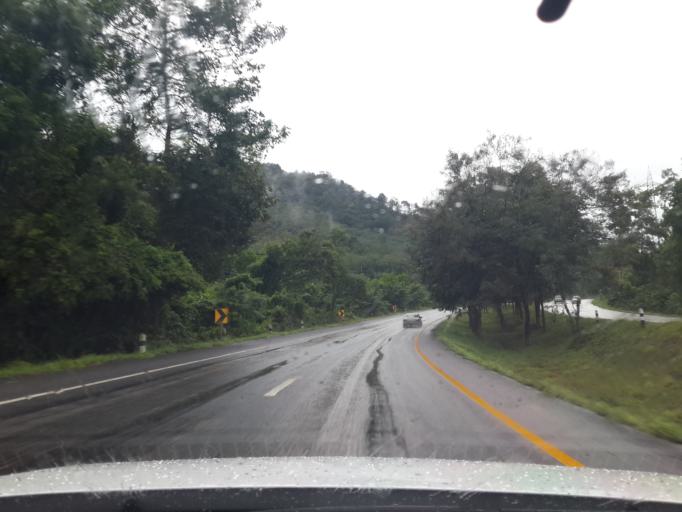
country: TH
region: Songkhla
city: Na Mom
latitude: 6.9897
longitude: 100.6181
